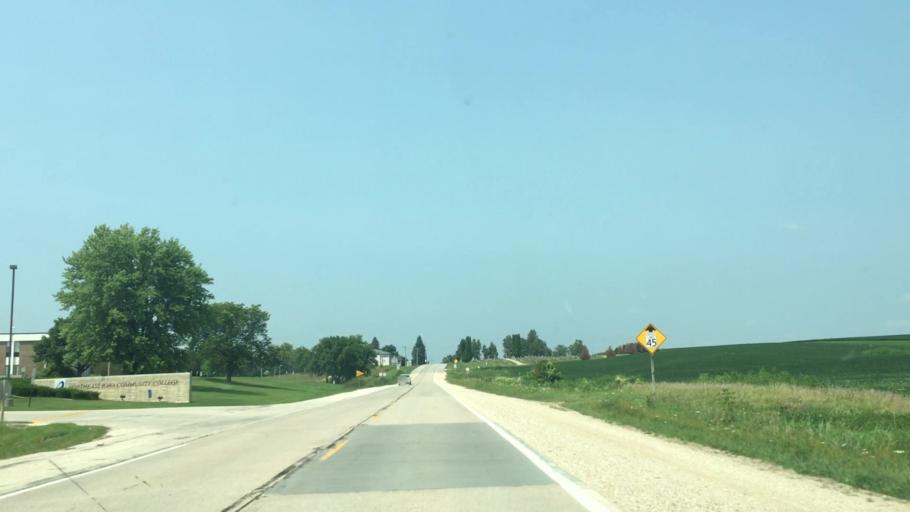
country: US
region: Iowa
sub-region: Winneshiek County
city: Decorah
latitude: 43.1732
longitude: -91.8644
